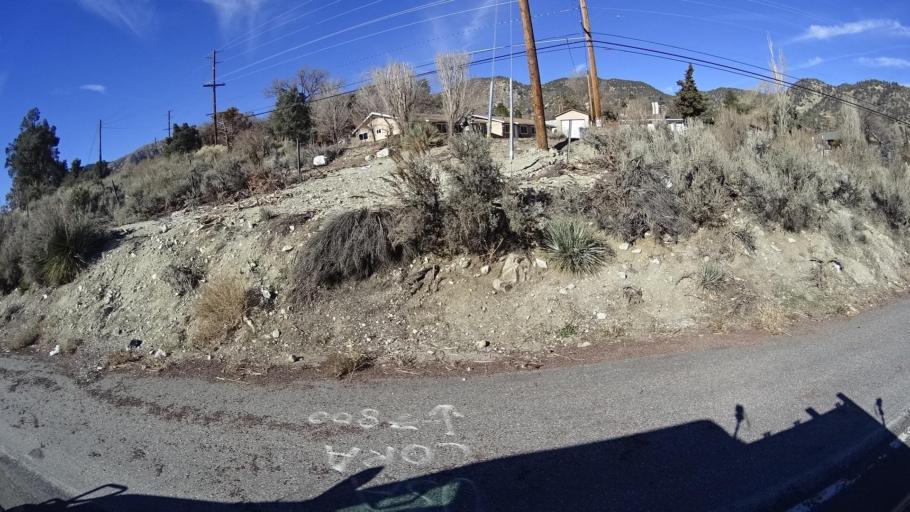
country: US
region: California
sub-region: Kern County
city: Frazier Park
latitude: 34.8202
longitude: -118.9359
